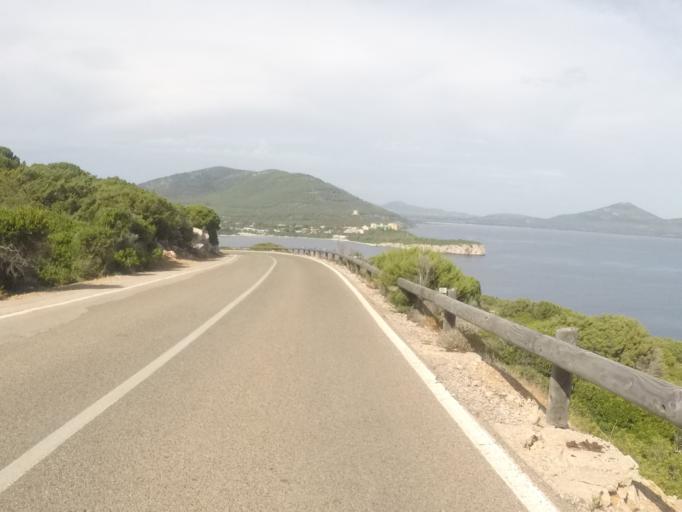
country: IT
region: Sardinia
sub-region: Provincia di Sassari
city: Alghero
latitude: 40.5711
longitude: 8.1629
